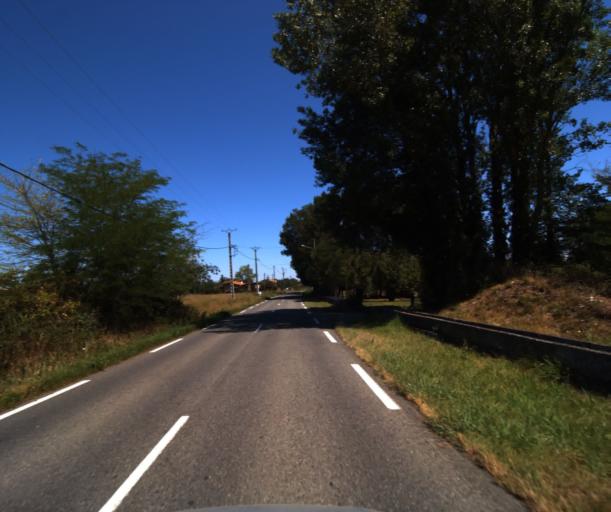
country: FR
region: Midi-Pyrenees
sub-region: Departement de la Haute-Garonne
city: Seysses
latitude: 43.4770
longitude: 1.3041
